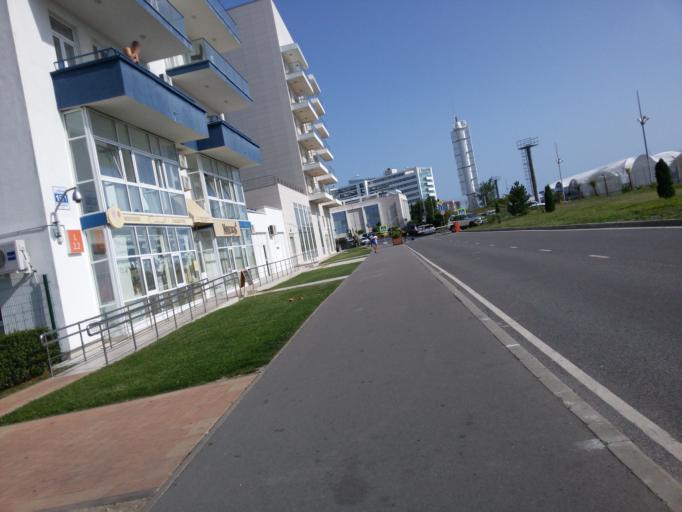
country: RU
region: Krasnodarskiy
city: Adler
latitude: 43.4116
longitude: 39.9346
